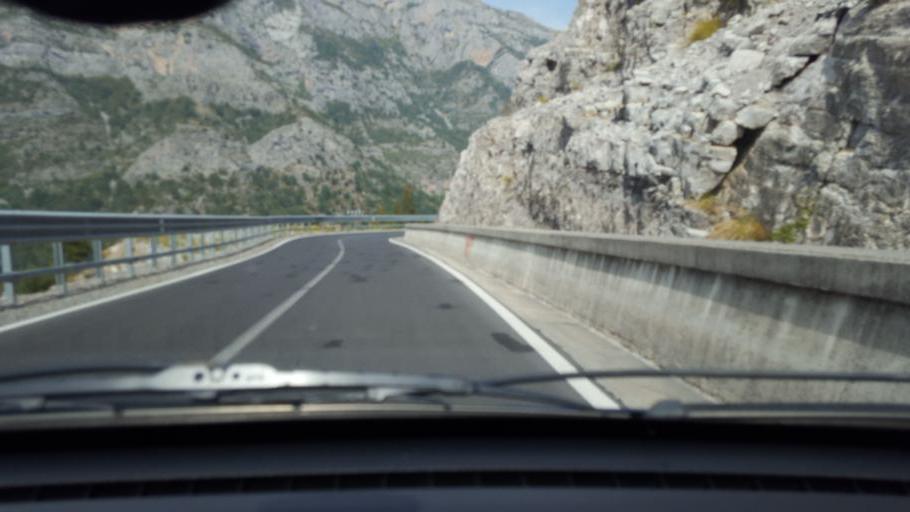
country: AL
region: Shkoder
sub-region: Rrethi i Malesia e Madhe
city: Kastrat
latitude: 42.4203
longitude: 19.5034
